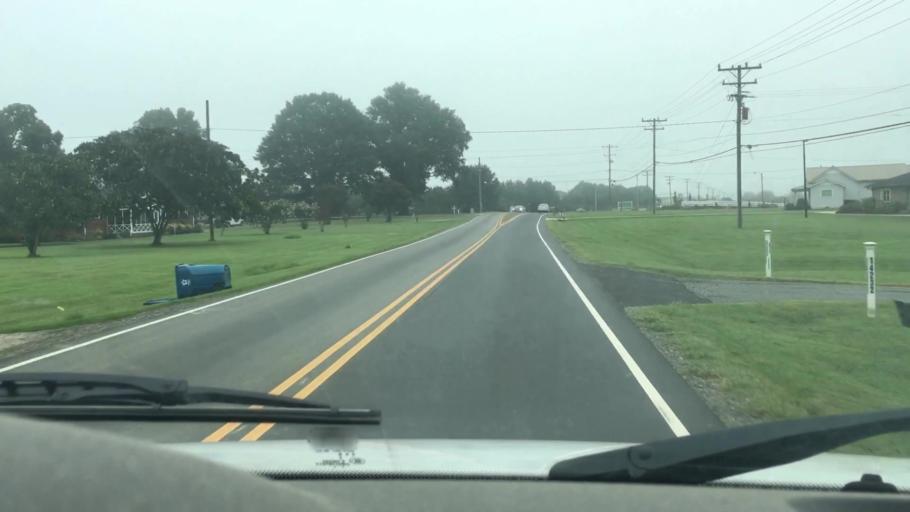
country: US
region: North Carolina
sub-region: Mecklenburg County
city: Huntersville
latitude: 35.3960
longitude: -80.7709
